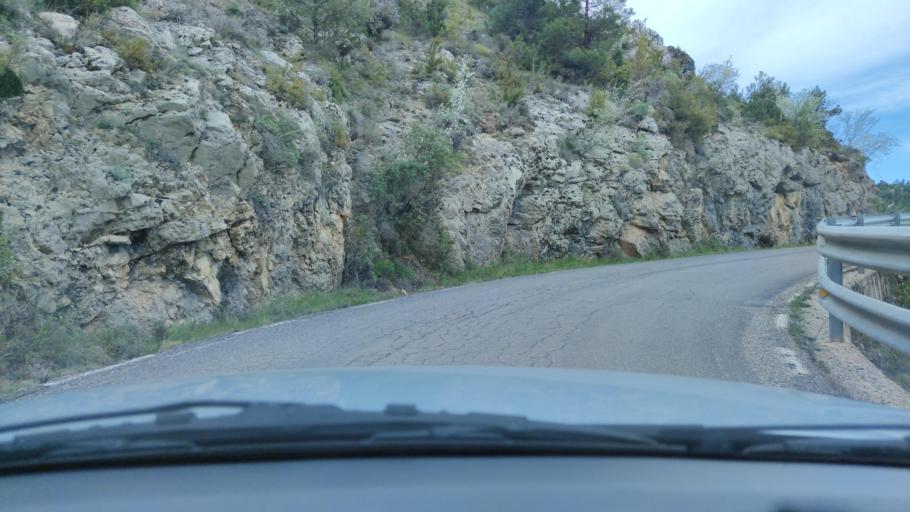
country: ES
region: Catalonia
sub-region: Provincia de Lleida
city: Coll de Nargo
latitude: 42.2437
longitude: 1.3714
